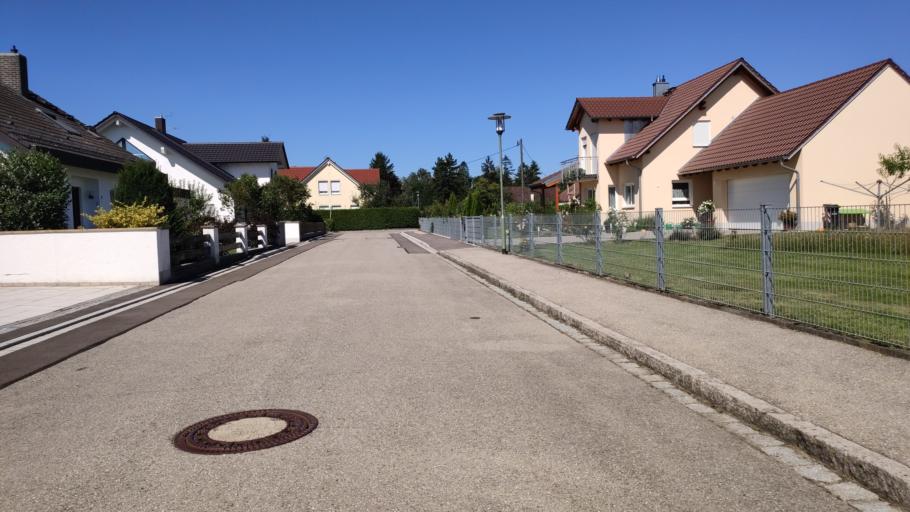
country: DE
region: Bavaria
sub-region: Swabia
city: Kleinaitingen
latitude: 48.2145
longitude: 10.8418
